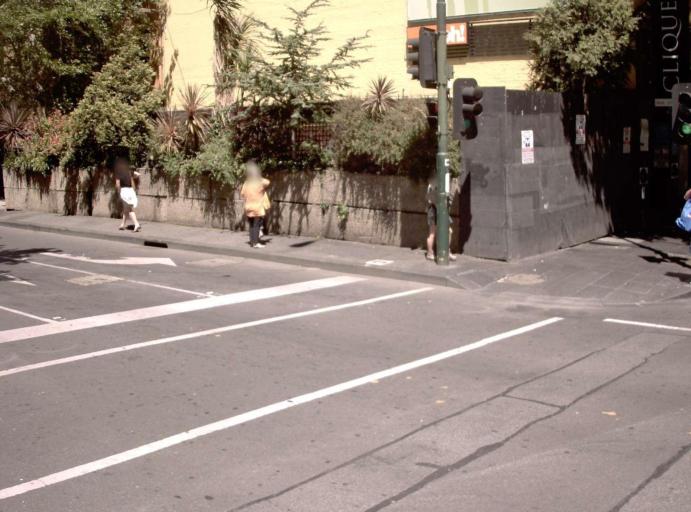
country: AU
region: Victoria
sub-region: Melbourne
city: Southbank
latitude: -37.8194
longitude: 144.9572
